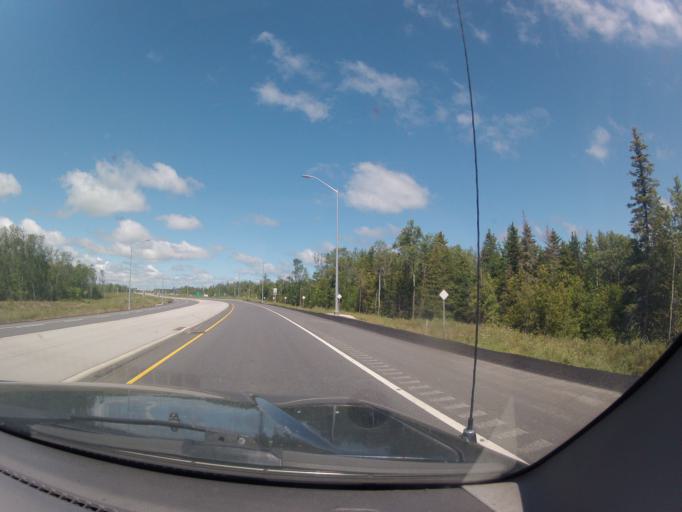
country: CA
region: Ontario
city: Wasaga Beach
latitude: 44.4603
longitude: -80.1078
